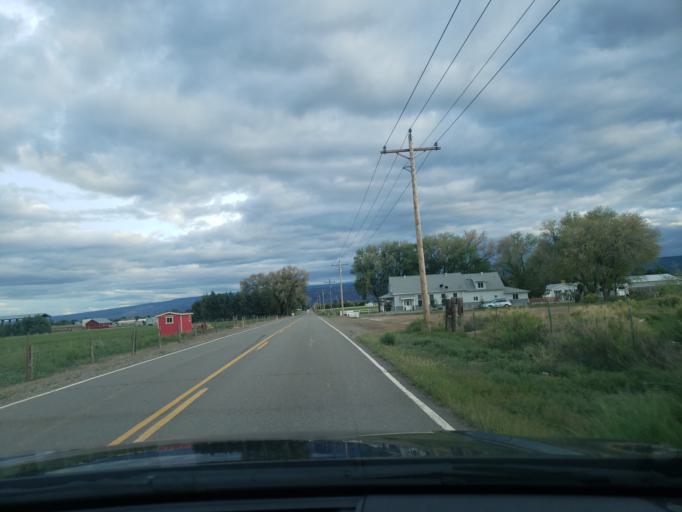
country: US
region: Colorado
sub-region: Mesa County
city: Fruita
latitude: 39.2198
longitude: -108.7011
